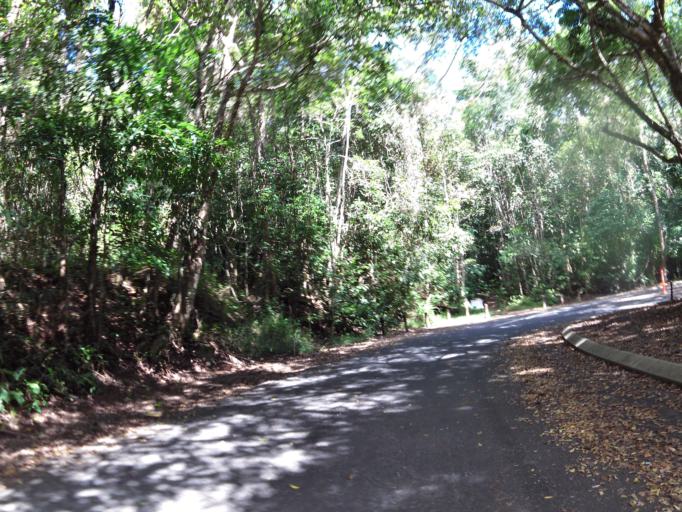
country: AU
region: Queensland
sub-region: Cairns
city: Woree
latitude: -16.9624
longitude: 145.6800
